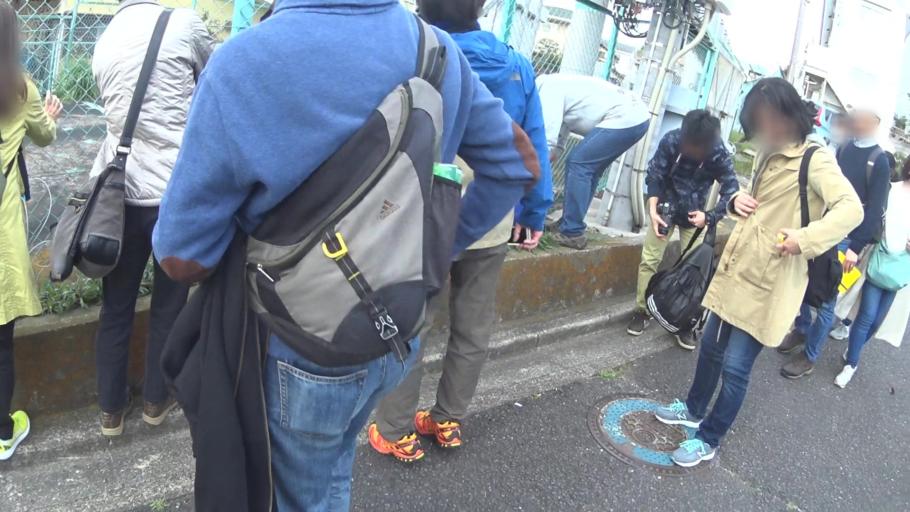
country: JP
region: Kanagawa
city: Kamakura
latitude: 35.3219
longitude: 139.5088
